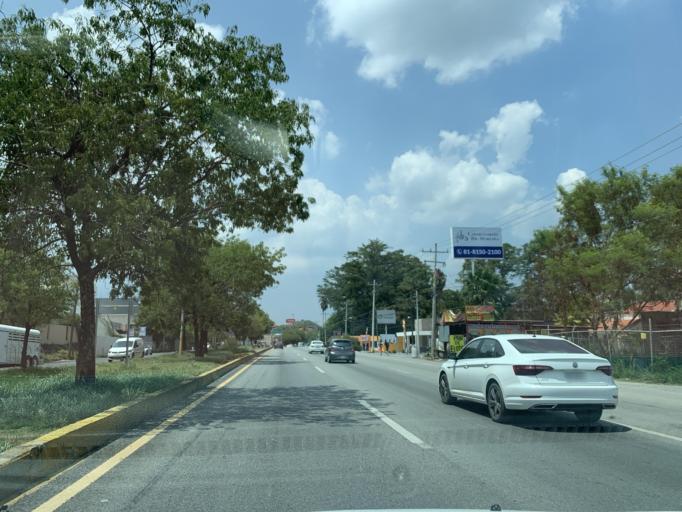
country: MX
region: Nuevo Leon
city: Santiago
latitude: 25.4212
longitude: -100.1451
